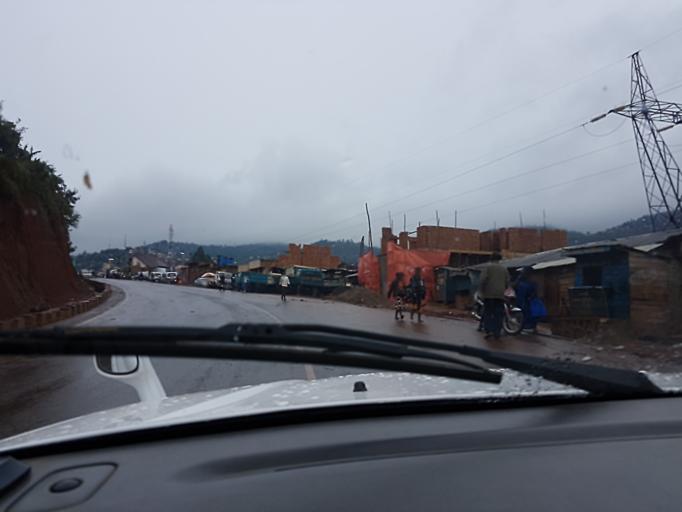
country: CD
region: South Kivu
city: Bukavu
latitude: -2.5189
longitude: 28.8551
